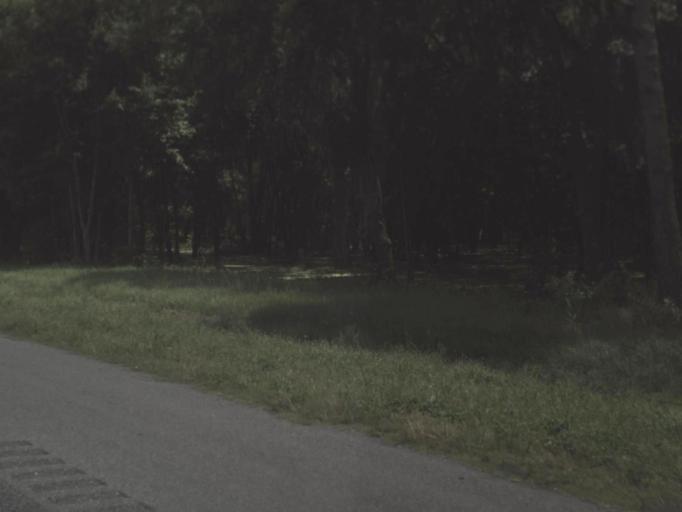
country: US
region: Florida
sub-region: Hamilton County
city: Jasper
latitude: 30.4783
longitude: -82.9821
